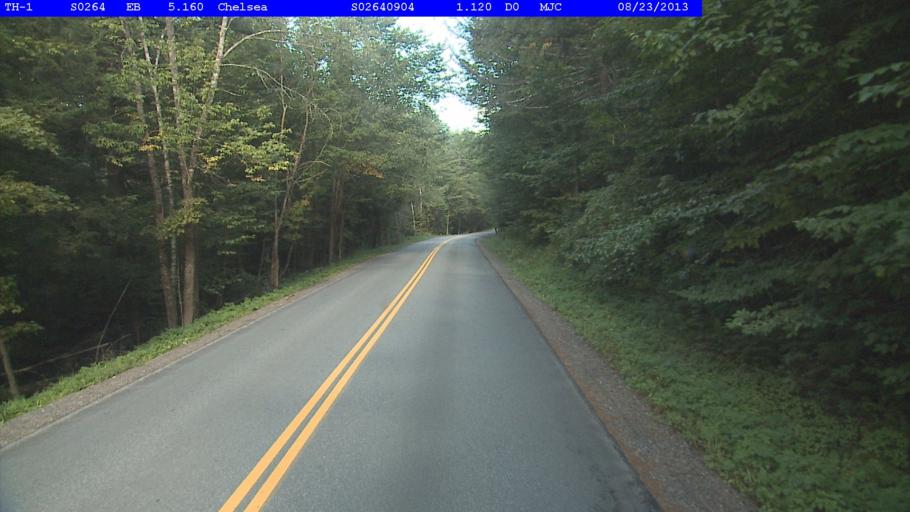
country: US
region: Vermont
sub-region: Orange County
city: Chelsea
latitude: 43.9721
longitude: -72.4912
